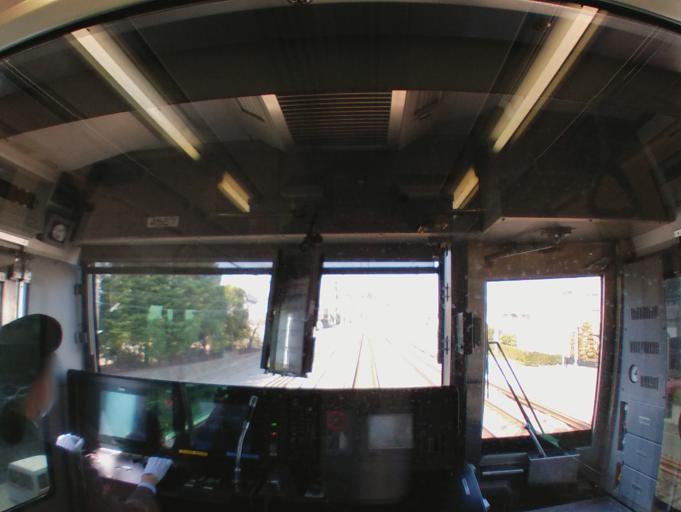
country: JP
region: Tokyo
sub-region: Machida-shi
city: Machida
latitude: 35.6066
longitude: 139.4800
